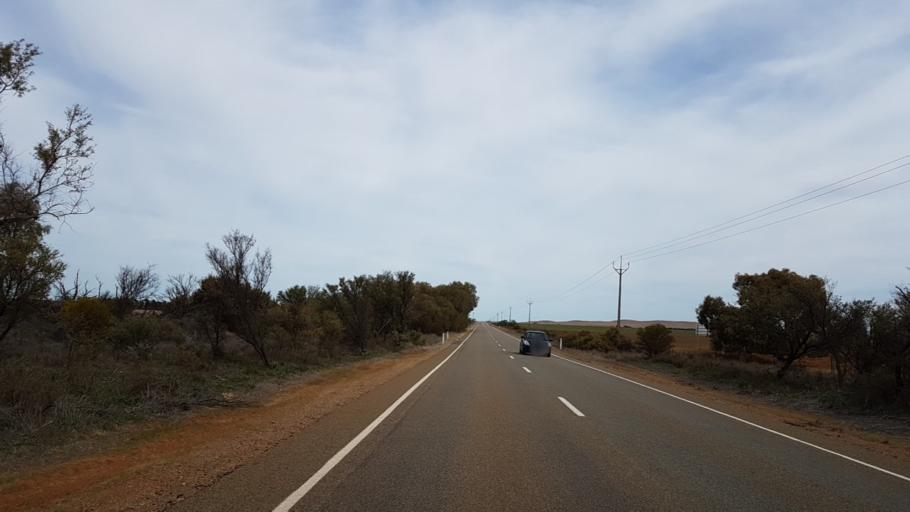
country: AU
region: South Australia
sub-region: Peterborough
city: Peterborough
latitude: -32.9970
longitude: 138.7825
